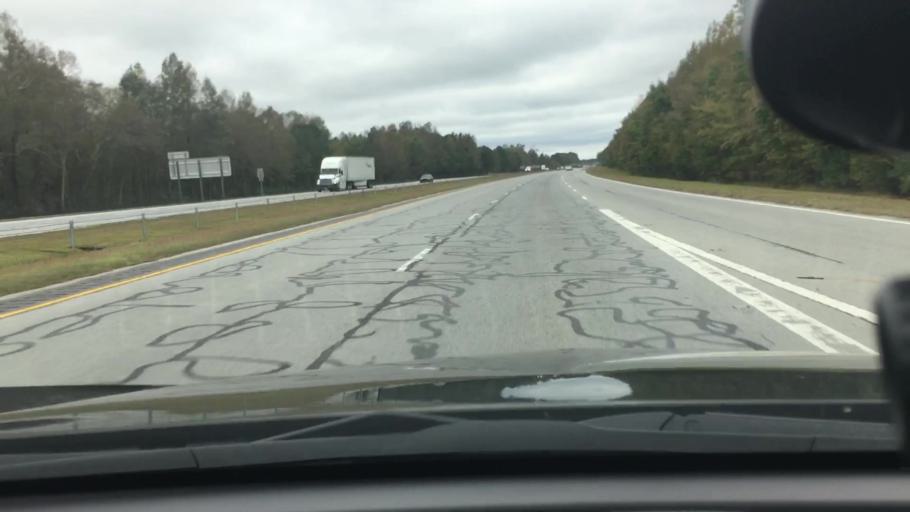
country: US
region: North Carolina
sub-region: Pitt County
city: Farmville
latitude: 35.6009
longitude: -77.5615
